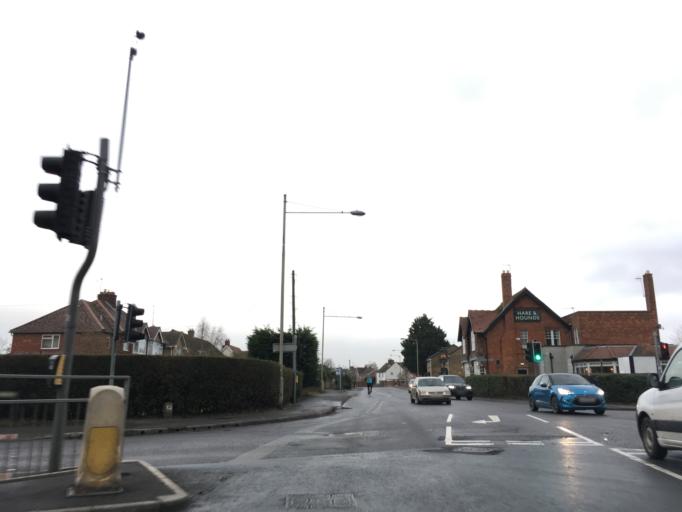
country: GB
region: England
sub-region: Gloucestershire
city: Churchdown
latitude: 51.8882
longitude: -2.1864
